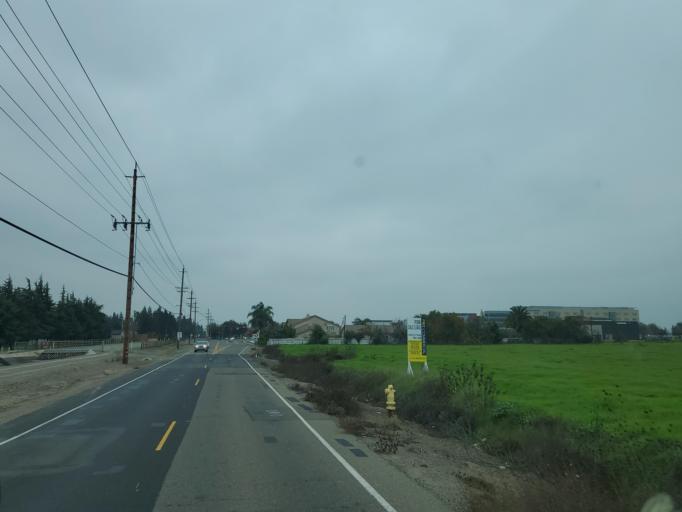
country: US
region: California
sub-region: Stanislaus County
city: Salida
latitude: 37.7040
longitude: -121.0469
